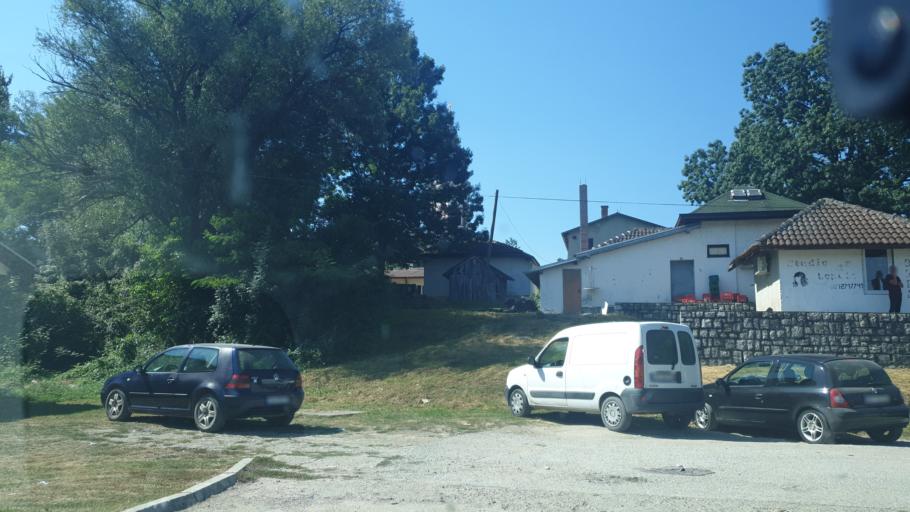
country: RS
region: Central Serbia
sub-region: Kolubarski Okrug
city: Mionica
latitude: 44.2533
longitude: 20.0864
